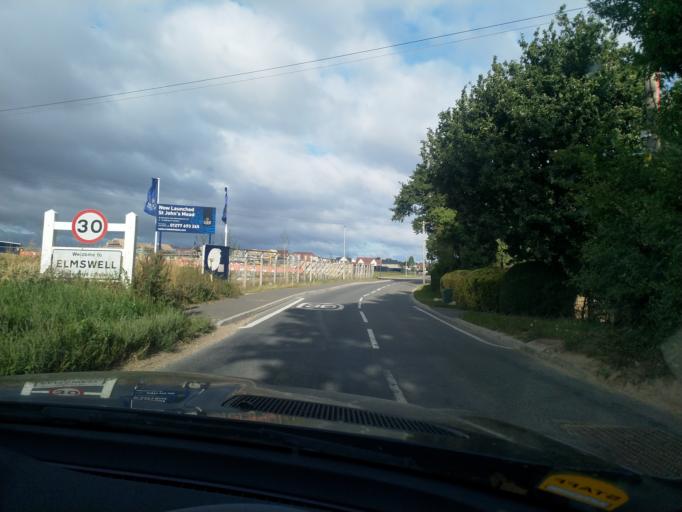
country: GB
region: England
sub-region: Suffolk
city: Elmswell
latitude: 52.2308
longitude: 0.9236
